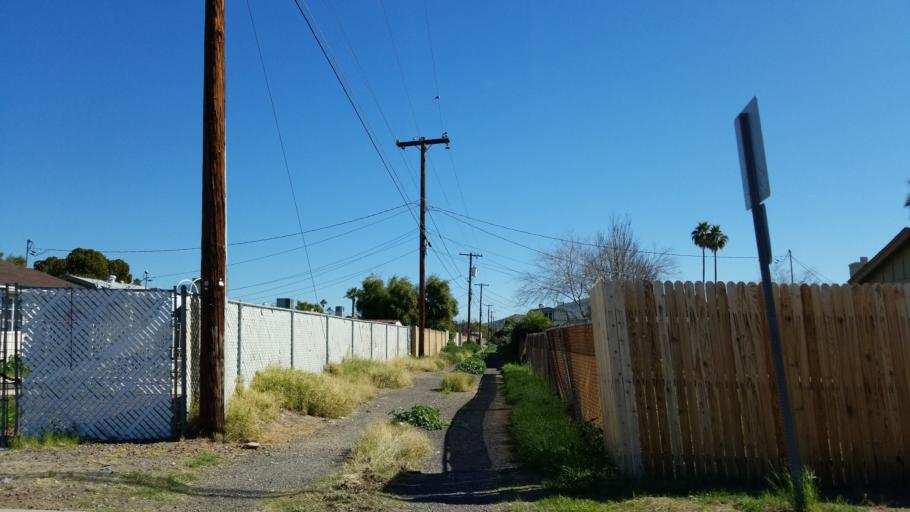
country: US
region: Arizona
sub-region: Maricopa County
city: Glendale
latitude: 33.6004
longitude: -112.1253
